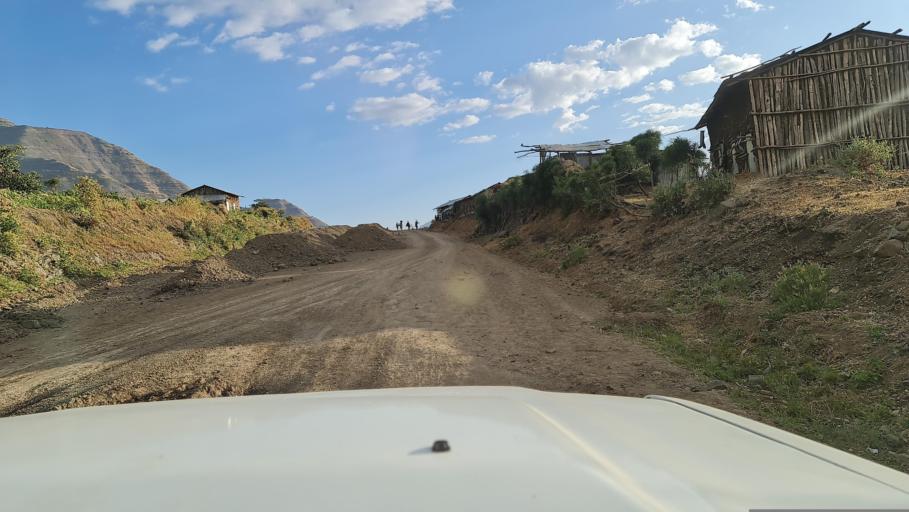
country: ET
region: Amhara
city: Debark'
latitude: 13.0398
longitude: 38.0385
